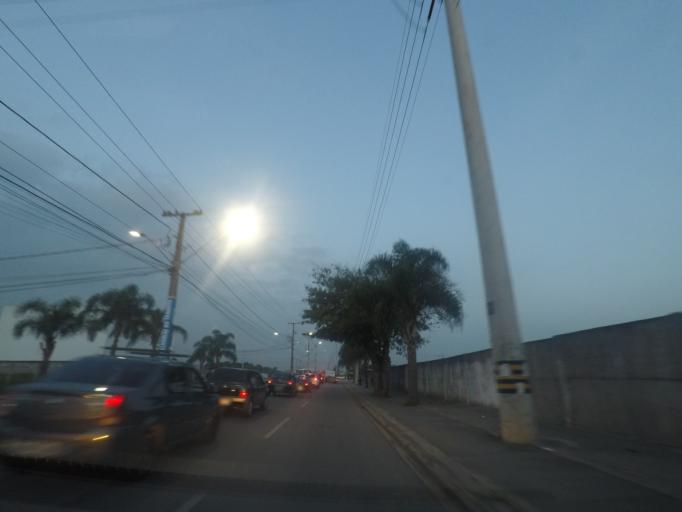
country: BR
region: Parana
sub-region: Pinhais
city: Pinhais
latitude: -25.4536
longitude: -49.1728
